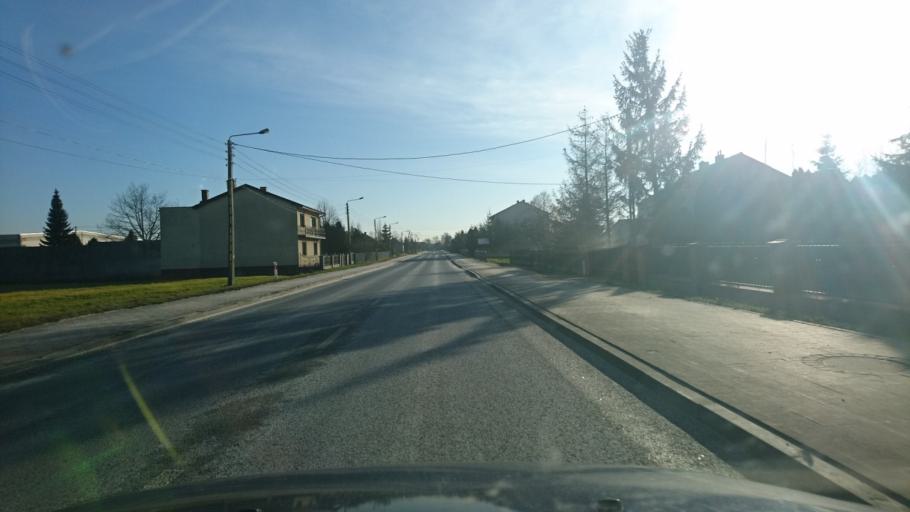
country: PL
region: Silesian Voivodeship
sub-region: Powiat klobucki
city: Starokrzepice
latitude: 51.0089
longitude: 18.6575
